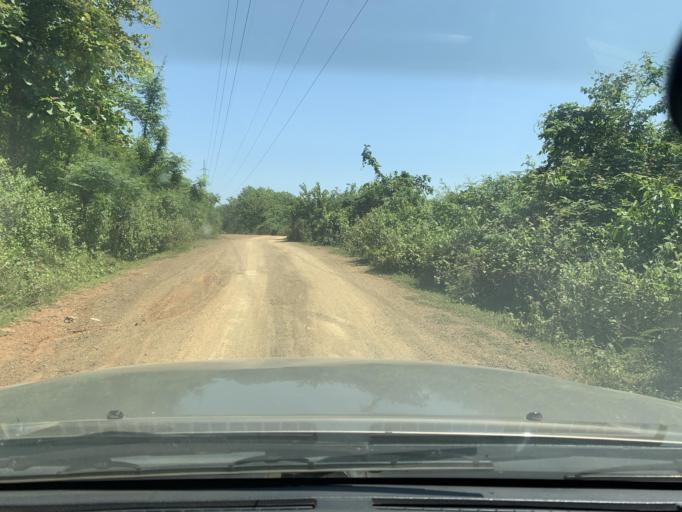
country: LA
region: Louangphabang
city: Louangphabang
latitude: 19.9036
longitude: 102.2193
